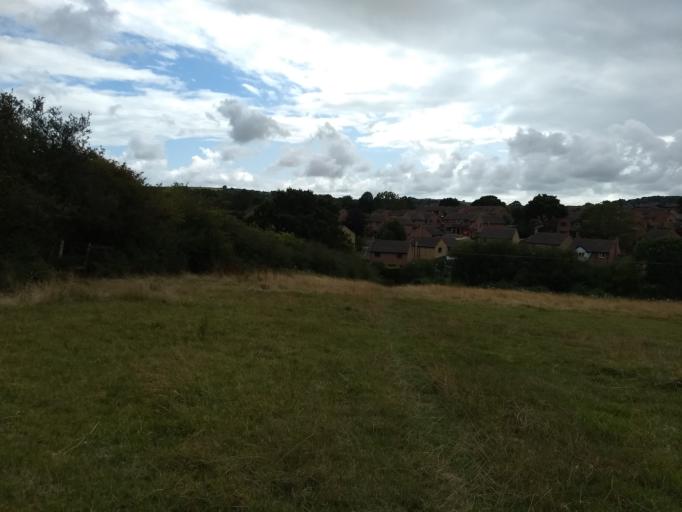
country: GB
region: England
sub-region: Isle of Wight
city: Newport
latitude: 50.7040
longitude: -1.3023
